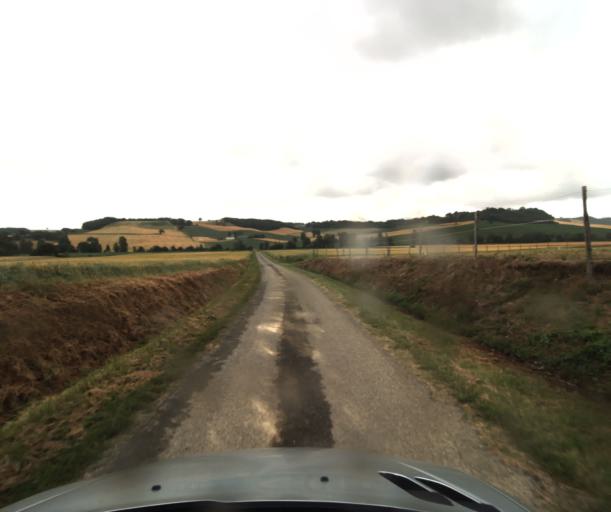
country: FR
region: Midi-Pyrenees
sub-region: Departement du Tarn-et-Garonne
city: Lavit
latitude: 43.9508
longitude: 0.9334
